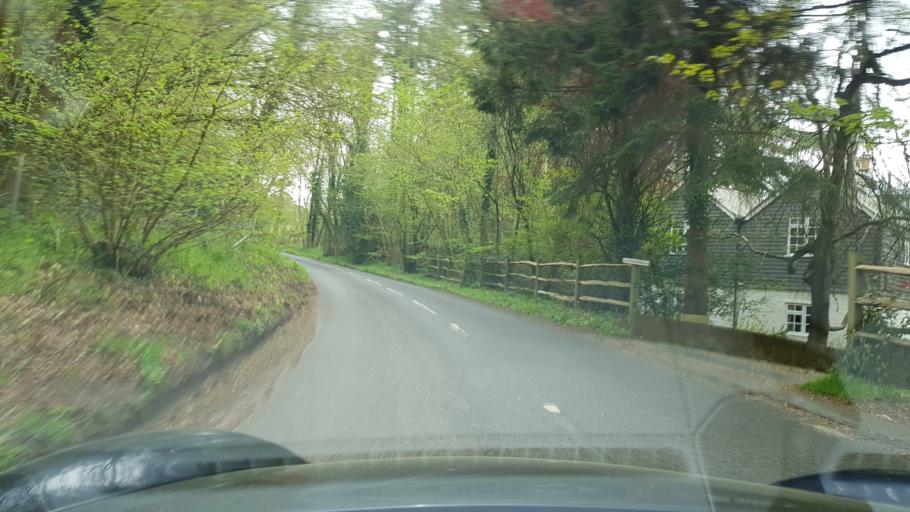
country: GB
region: England
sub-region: Surrey
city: East Horsley
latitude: 51.2460
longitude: -0.4405
